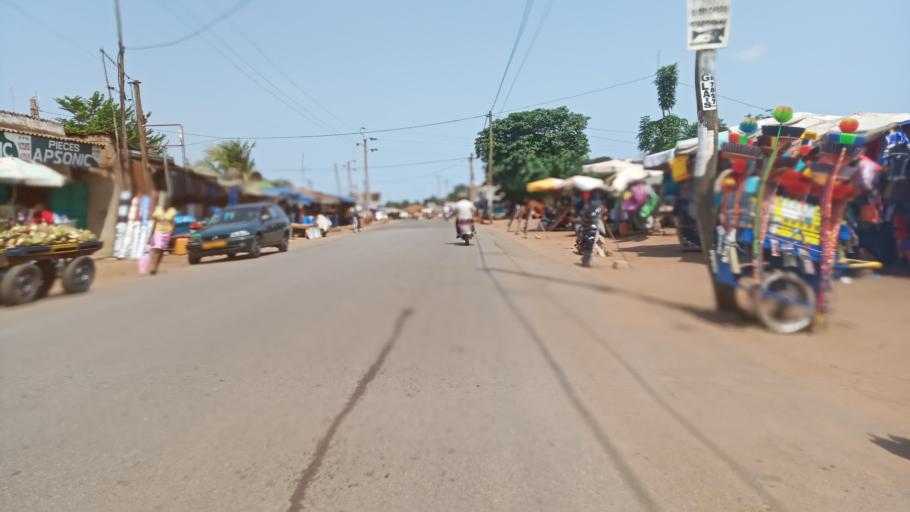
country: TG
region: Maritime
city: Lome
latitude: 6.2247
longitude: 1.2063
